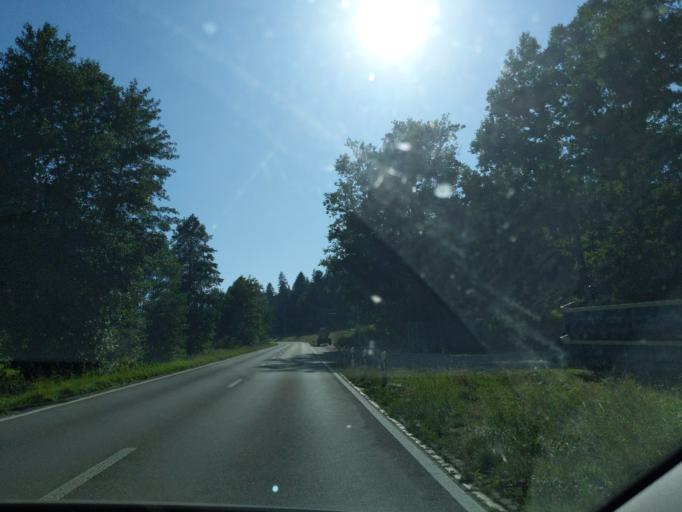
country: CH
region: Bern
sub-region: Oberaargau
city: Huttwil
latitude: 47.1238
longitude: 7.8730
